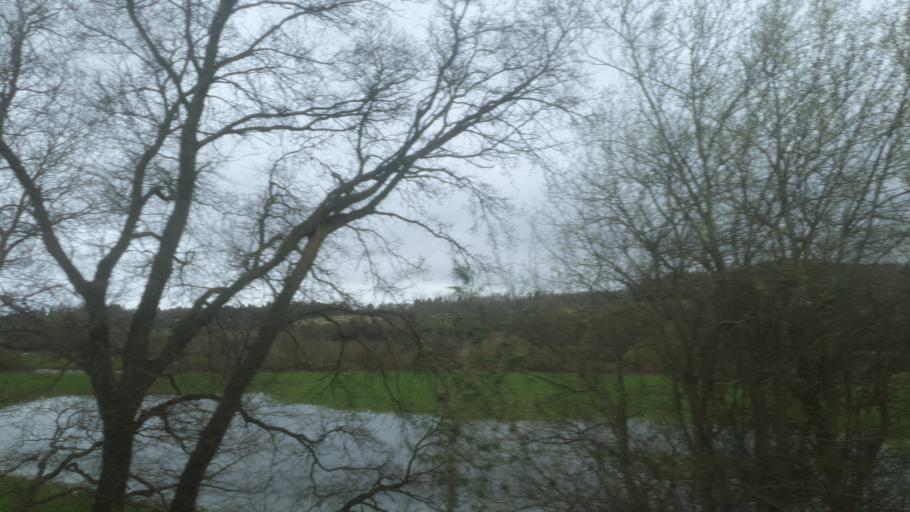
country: GB
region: England
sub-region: West Sussex
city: Pulborough
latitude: 50.9551
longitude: -0.5191
